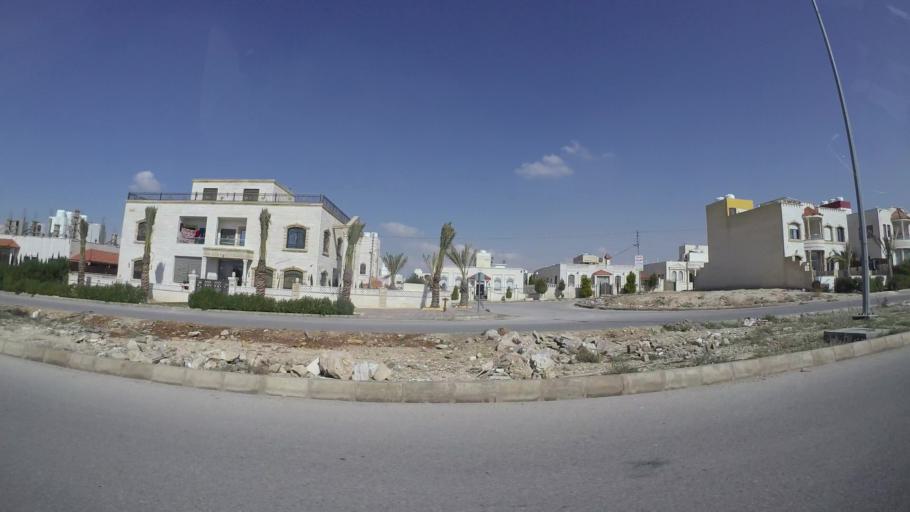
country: JO
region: Zarqa
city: Zarqa
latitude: 32.0562
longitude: 36.1148
